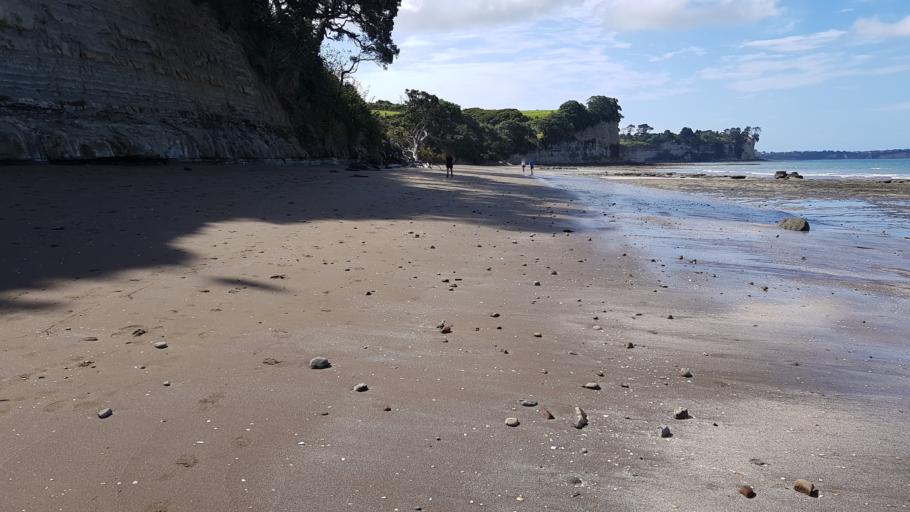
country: NZ
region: Auckland
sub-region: Auckland
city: Rothesay Bay
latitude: -36.6760
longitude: 174.7481
